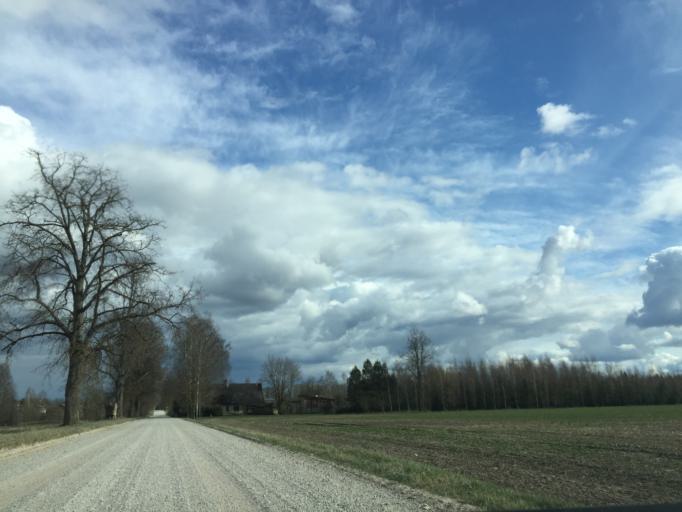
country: LV
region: Burtnieki
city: Matisi
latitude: 57.6027
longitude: 25.0852
